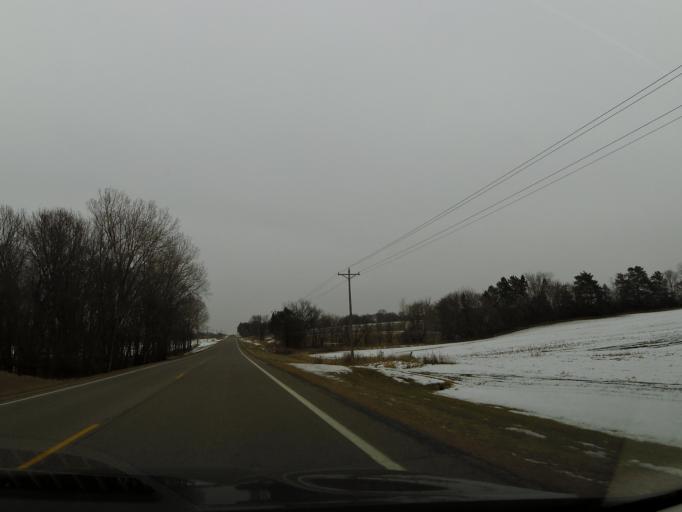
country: US
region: Minnesota
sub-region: Le Sueur County
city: New Prague
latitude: 44.6305
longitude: -93.5130
